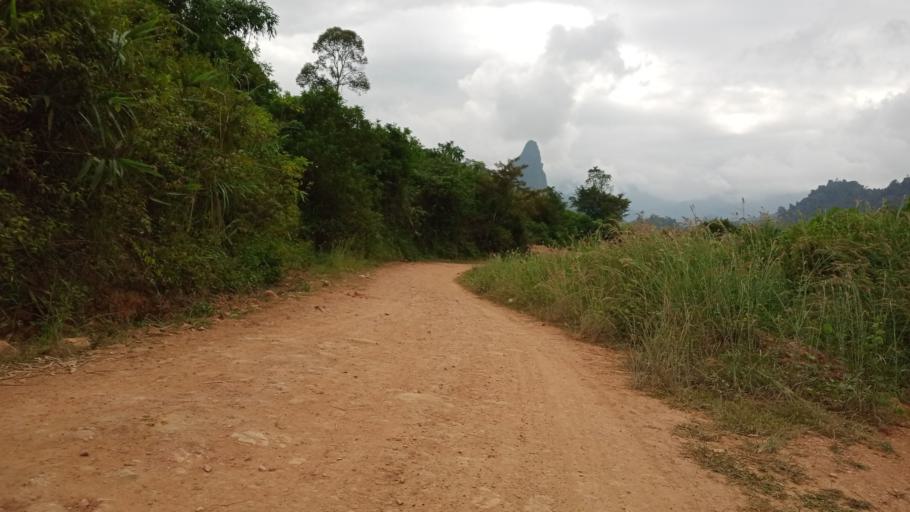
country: LA
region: Xiangkhoang
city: Phonsavan
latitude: 19.0887
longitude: 103.0064
